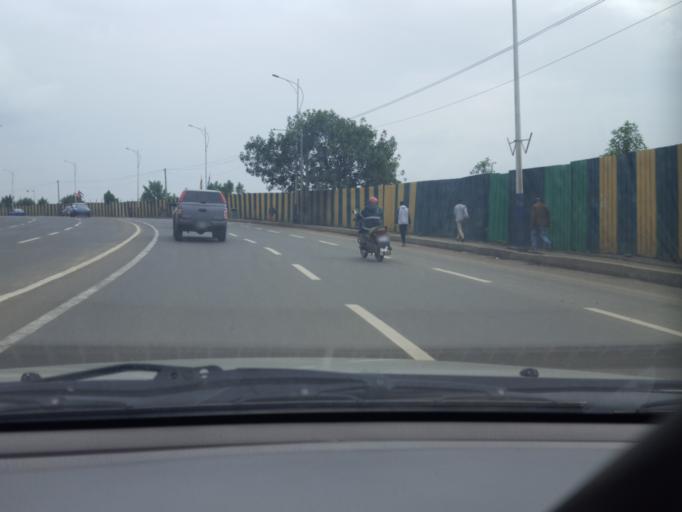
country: ET
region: Adis Abeba
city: Addis Ababa
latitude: 9.0252
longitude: 38.7614
